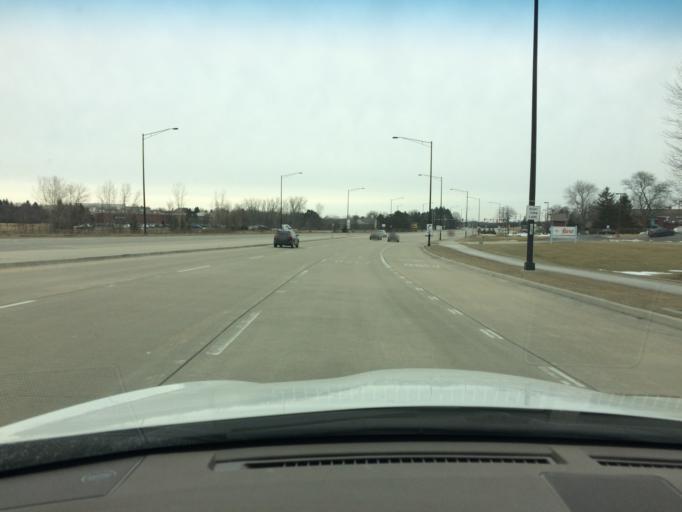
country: US
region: Illinois
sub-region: Cook County
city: South Barrington
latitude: 42.0686
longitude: -88.1443
